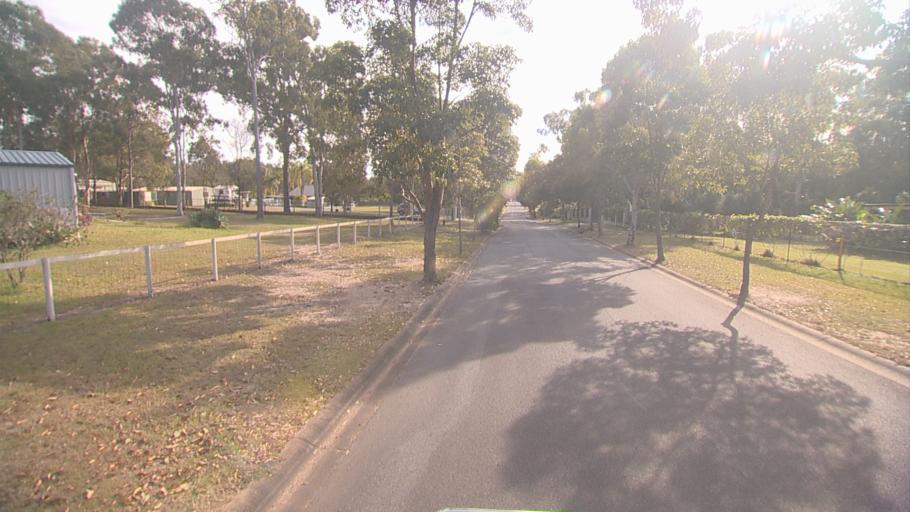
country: AU
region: Queensland
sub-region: Brisbane
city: Forest Lake
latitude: -27.6605
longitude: 153.0161
